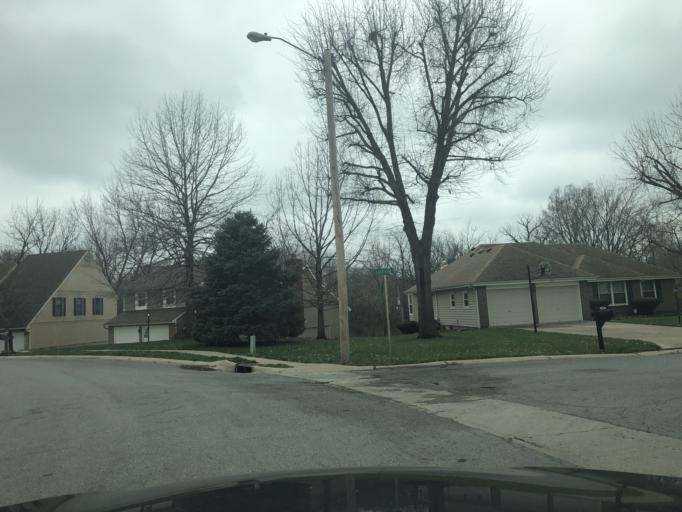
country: US
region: Kansas
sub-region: Leavenworth County
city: Leavenworth
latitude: 39.2857
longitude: -94.9150
